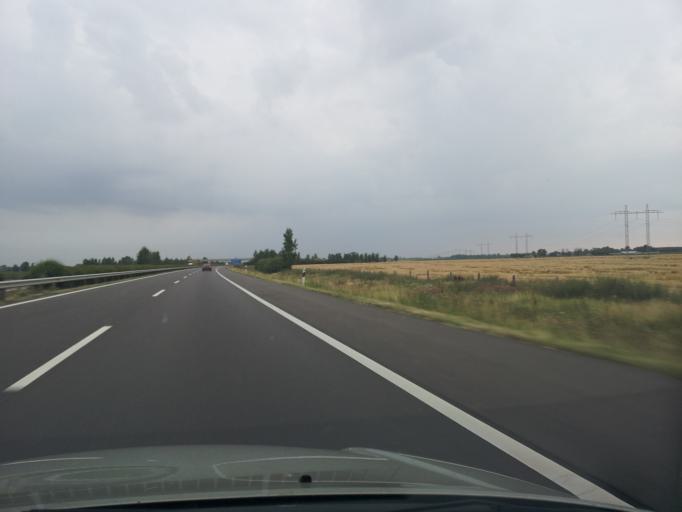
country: HU
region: Borsod-Abauj-Zemplen
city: Mezokeresztes
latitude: 47.8262
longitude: 20.7318
